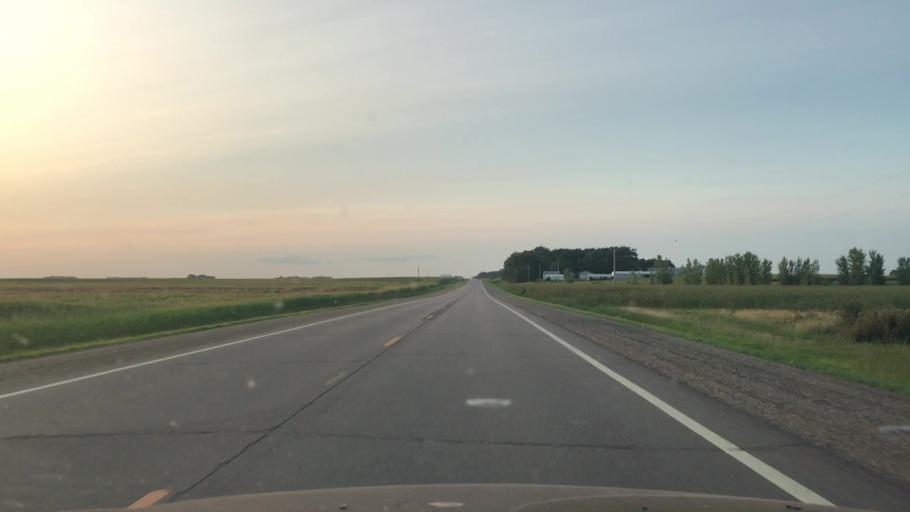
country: US
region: Minnesota
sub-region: Redwood County
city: Redwood Falls
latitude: 44.4426
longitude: -95.1178
